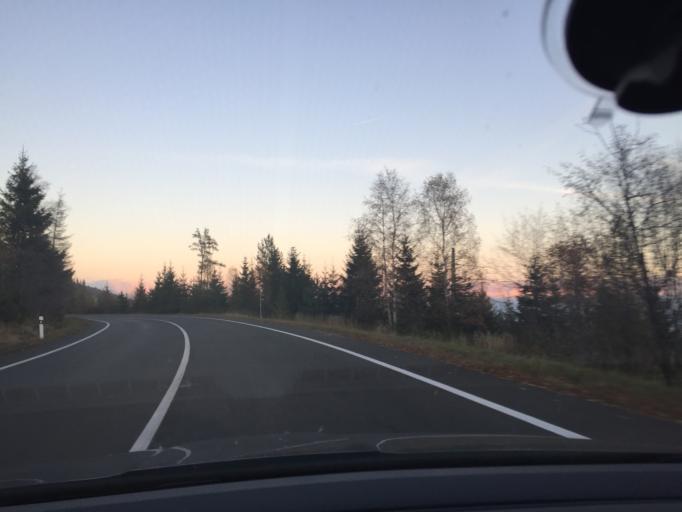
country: SK
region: Presovsky
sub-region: Okres Poprad
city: Vysoke Tatry
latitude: 49.1320
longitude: 20.2048
